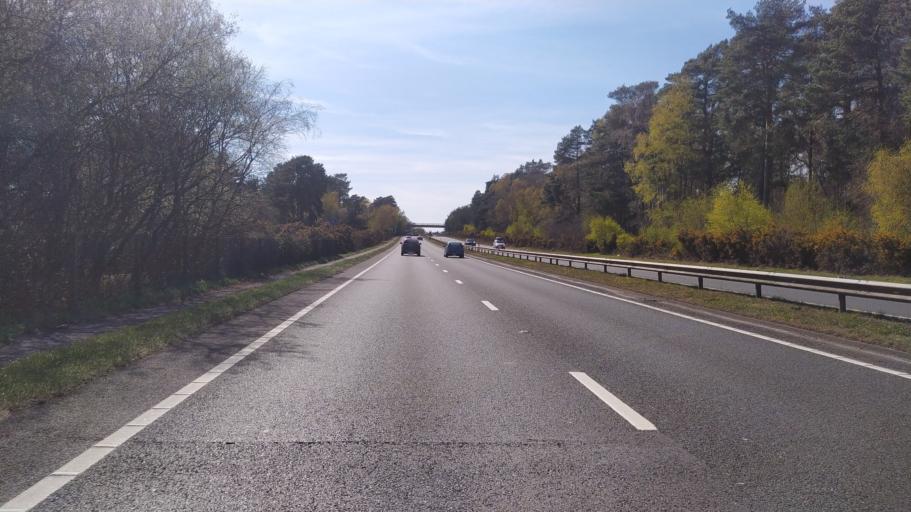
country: GB
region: England
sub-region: Hampshire
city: Bordon
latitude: 51.0758
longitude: -0.8530
